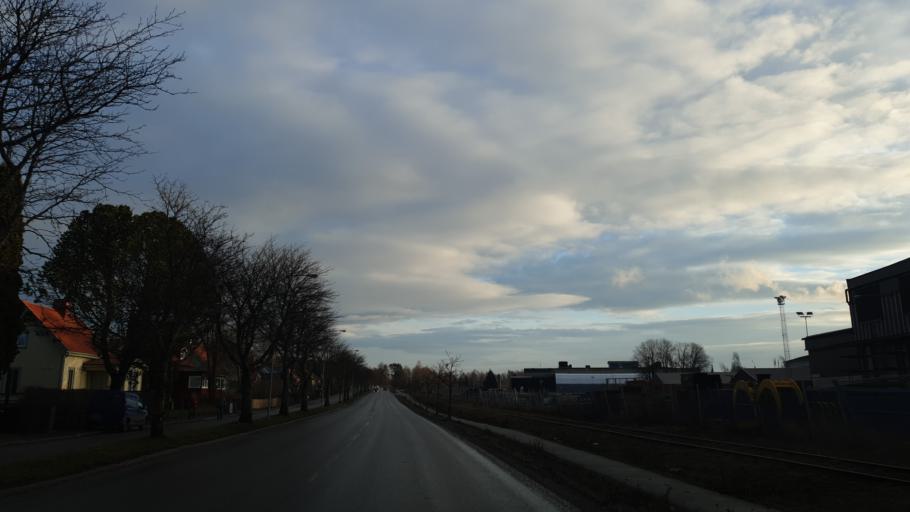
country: SE
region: Gaevleborg
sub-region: Hudiksvalls Kommun
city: Hudiksvall
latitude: 61.7247
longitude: 17.1323
